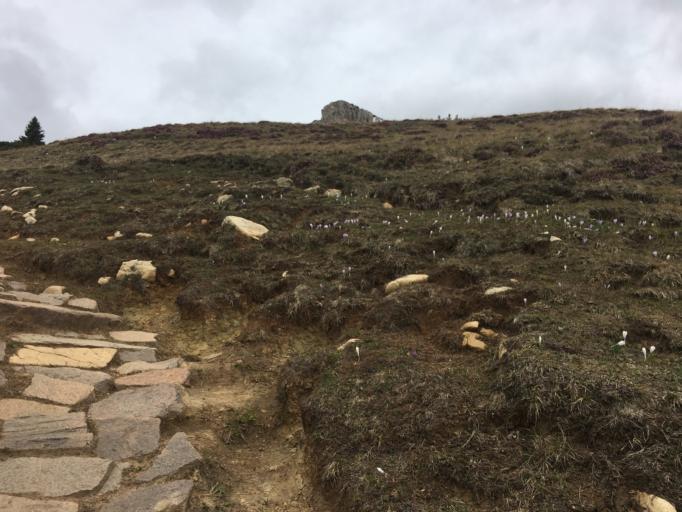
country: IT
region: Trentino-Alto Adige
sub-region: Provincia di Trento
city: Varena
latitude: 46.3488
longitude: 11.4473
